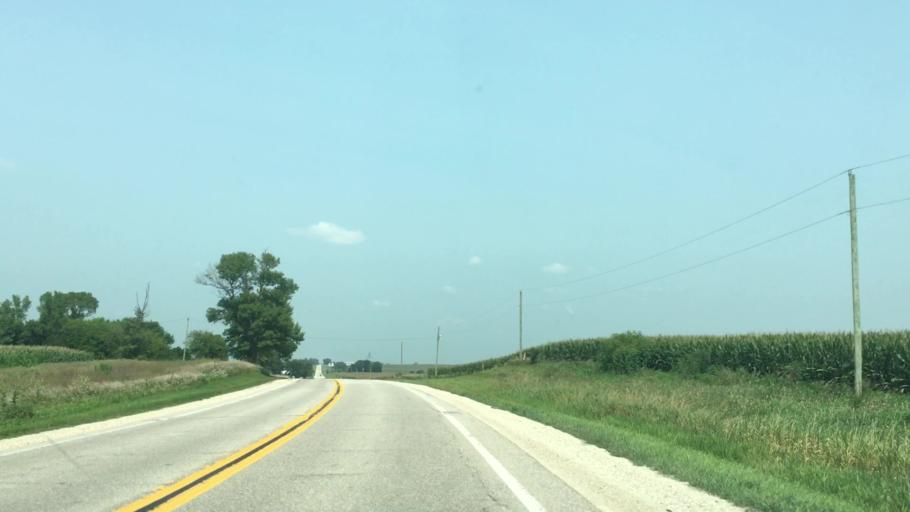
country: US
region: Iowa
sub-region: Benton County
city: Urbana
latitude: 42.2987
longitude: -91.8895
